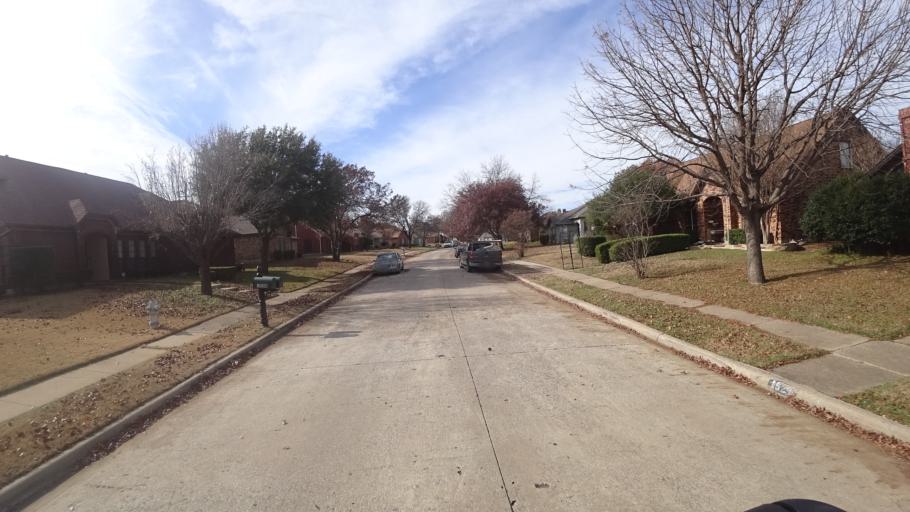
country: US
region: Texas
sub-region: Denton County
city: Highland Village
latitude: 33.0621
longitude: -97.0376
